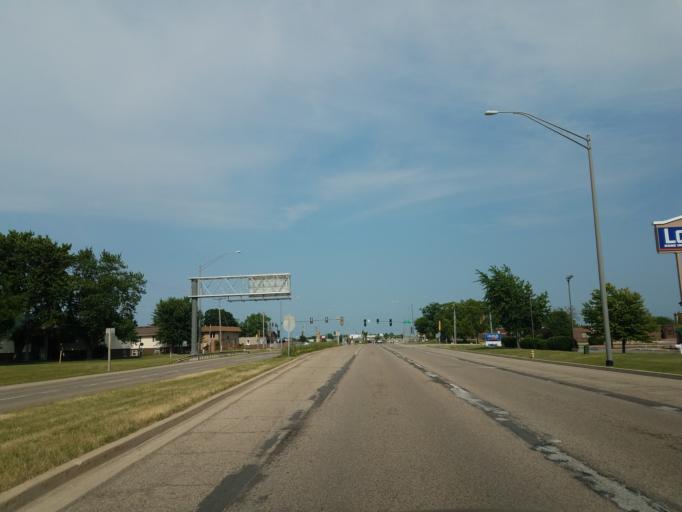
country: US
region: Illinois
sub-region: McLean County
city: Bloomington
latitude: 40.4882
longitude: -88.9470
